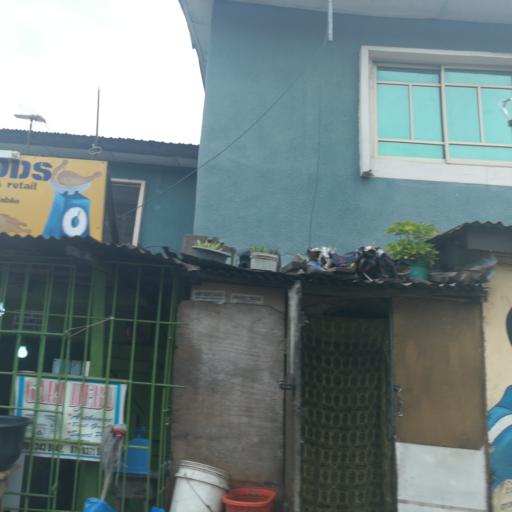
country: NG
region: Lagos
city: Ojota
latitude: 6.5875
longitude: 3.3824
